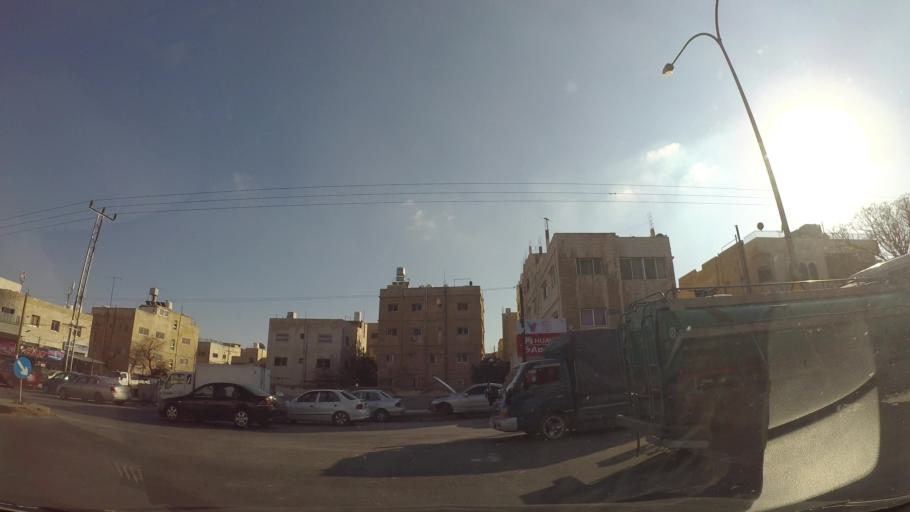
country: JO
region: Amman
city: Amman
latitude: 31.9745
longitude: 35.9645
